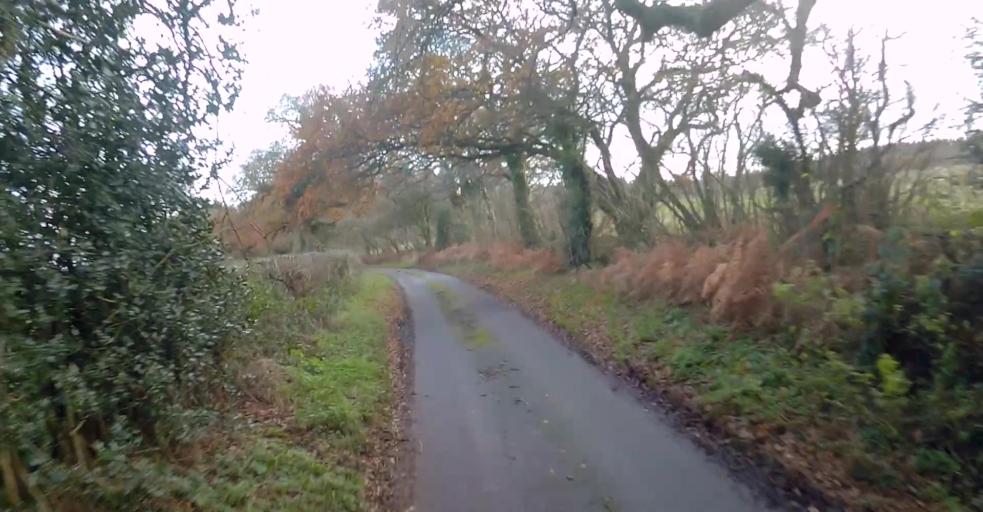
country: GB
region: England
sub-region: Hampshire
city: Basingstoke
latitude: 51.1994
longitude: -1.0714
